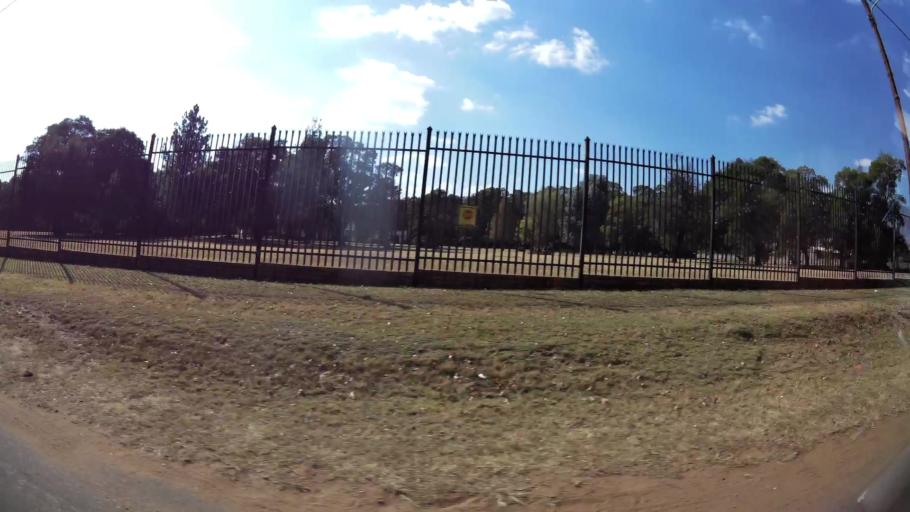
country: ZA
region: Gauteng
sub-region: Ekurhuleni Metropolitan Municipality
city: Benoni
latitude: -26.0863
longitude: 28.3257
